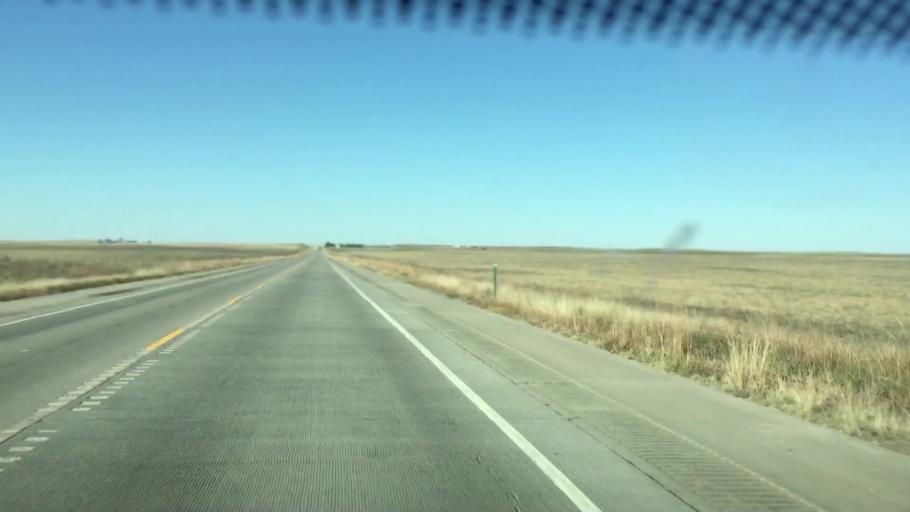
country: US
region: Colorado
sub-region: Kiowa County
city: Eads
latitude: 38.7070
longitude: -102.7758
